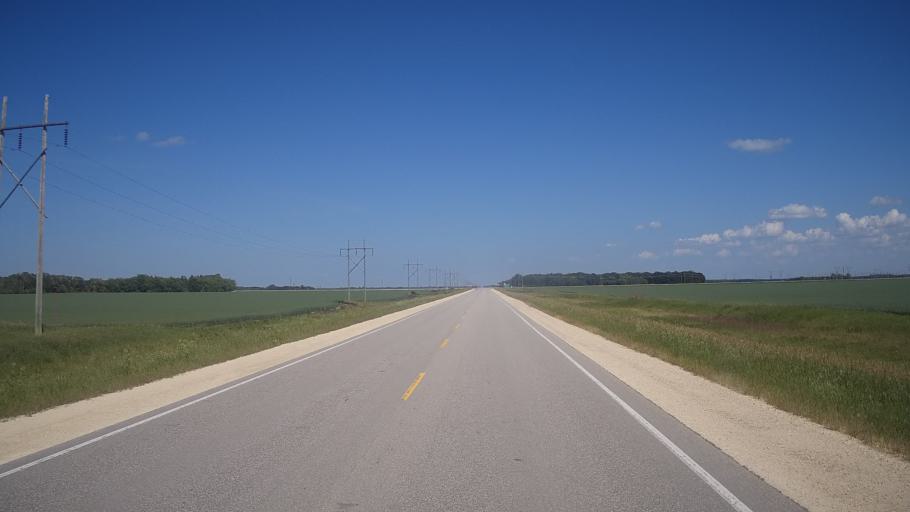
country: CA
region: Manitoba
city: Stonewall
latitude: 50.1227
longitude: -97.4464
